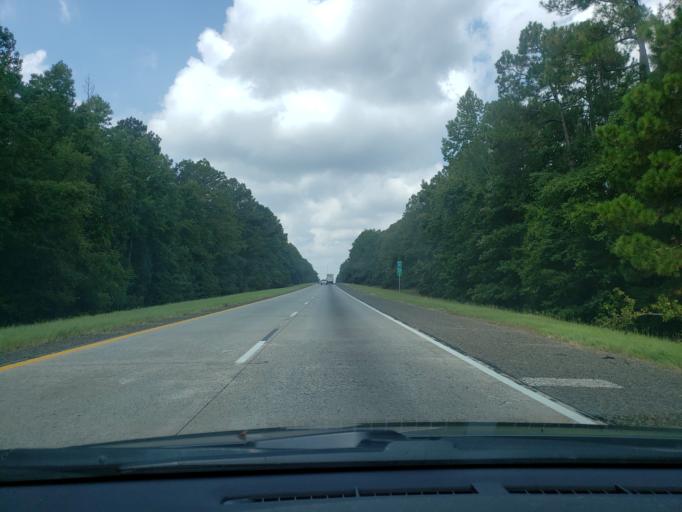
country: US
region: Georgia
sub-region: Treutlen County
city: Soperton
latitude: 32.4347
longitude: -82.6384
